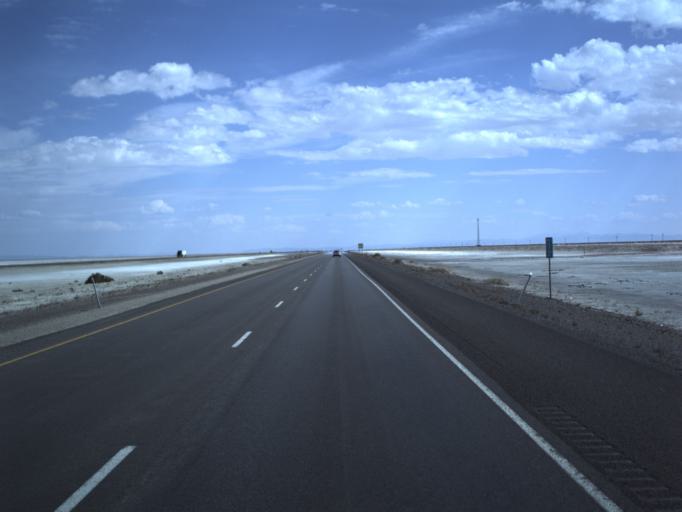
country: US
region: Utah
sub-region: Tooele County
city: Wendover
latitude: 40.7378
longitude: -113.8181
